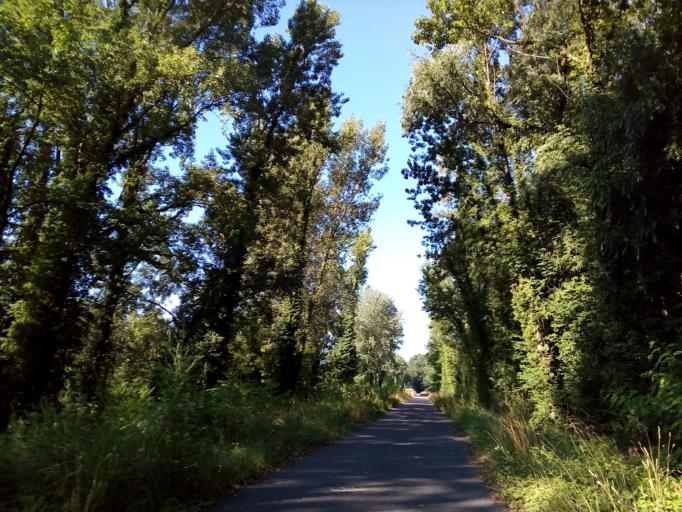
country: FR
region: Rhone-Alpes
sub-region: Departement de l'Isere
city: Le Versoud
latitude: 45.2257
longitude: 5.8475
